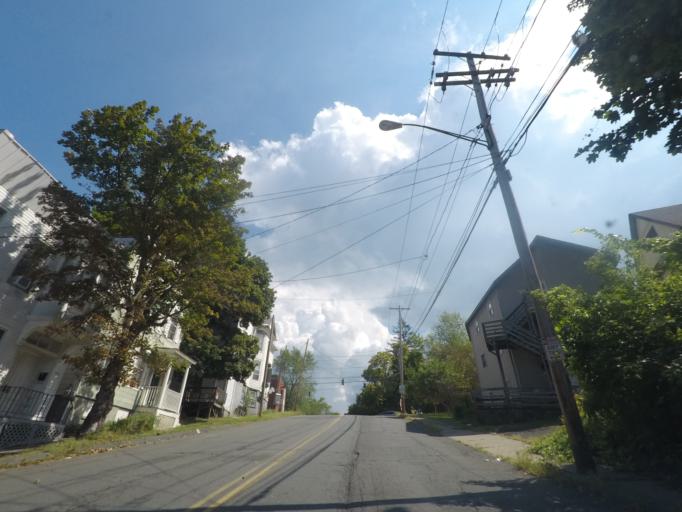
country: US
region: New York
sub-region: Albany County
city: Green Island
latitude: 42.7449
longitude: -73.6764
